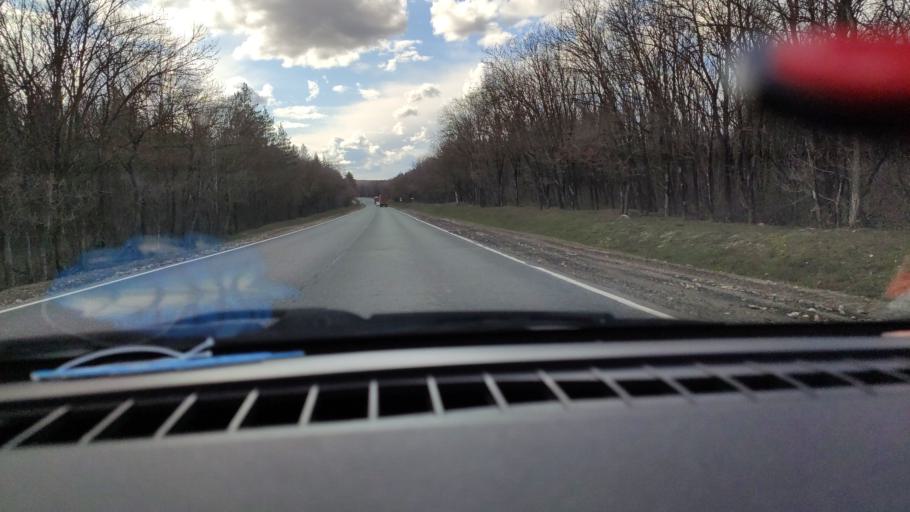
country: RU
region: Saratov
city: Vol'sk
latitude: 52.1060
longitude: 47.4318
